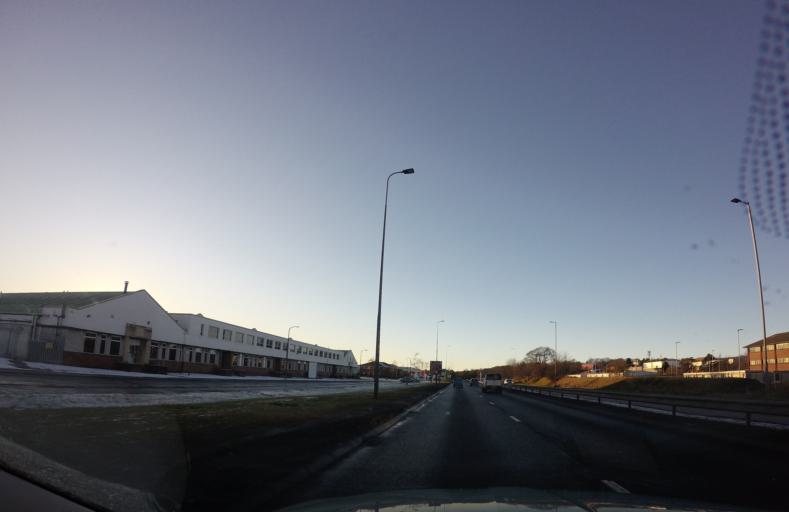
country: GB
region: Scotland
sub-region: Dundee City
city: Dundee
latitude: 56.4815
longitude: -3.0084
